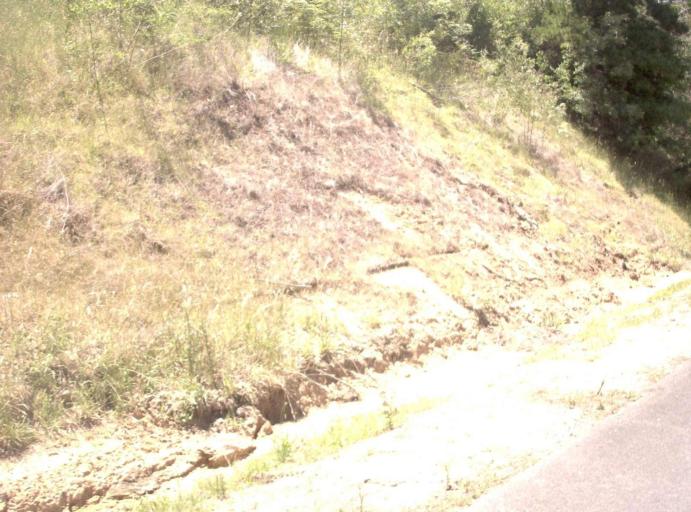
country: AU
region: Victoria
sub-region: East Gippsland
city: Lakes Entrance
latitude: -37.7568
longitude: 148.2744
